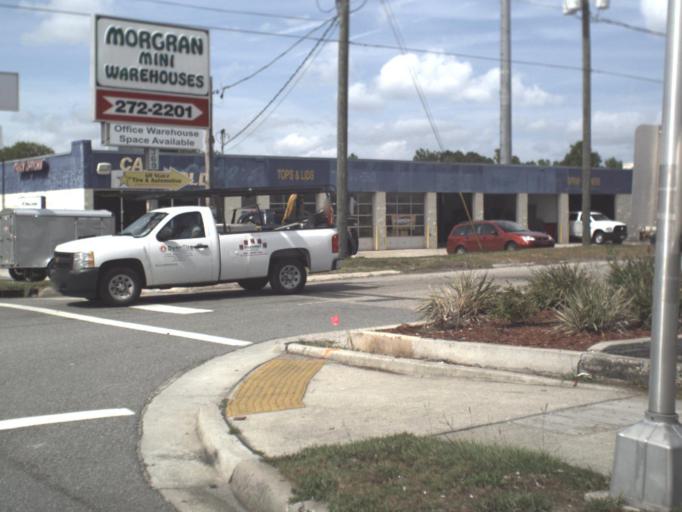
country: US
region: Florida
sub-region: Clay County
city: Bellair-Meadowbrook Terrace
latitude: 30.1661
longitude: -81.7475
